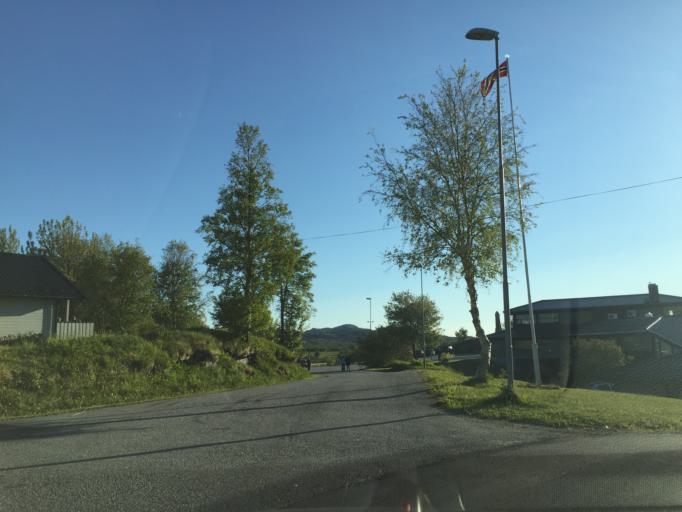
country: NO
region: Nordland
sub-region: Bodo
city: Loding
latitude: 67.2358
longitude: 14.6183
